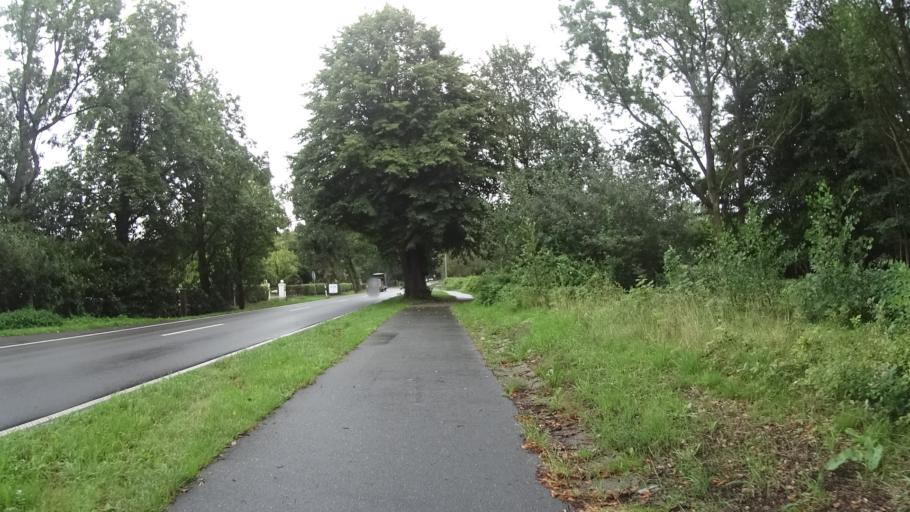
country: DE
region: Schleswig-Holstein
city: Alveslohe
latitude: 53.7849
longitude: 9.9449
